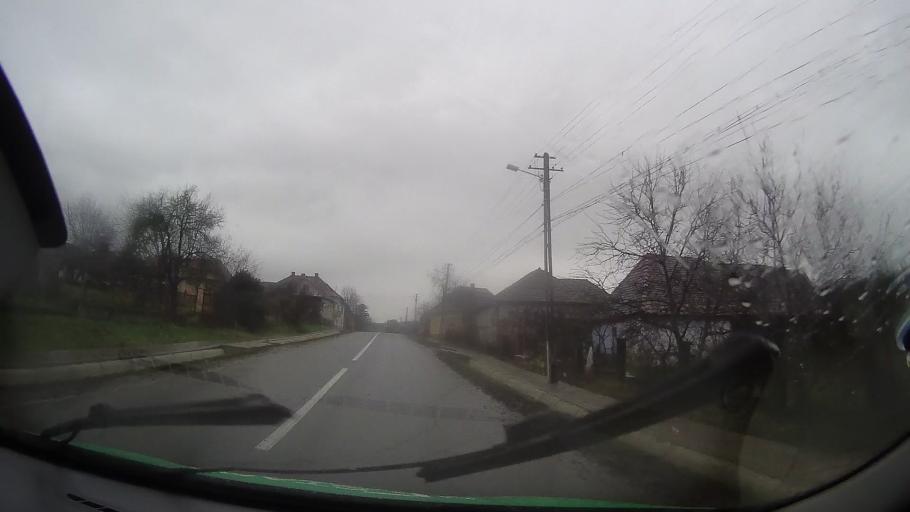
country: RO
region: Bistrita-Nasaud
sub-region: Comuna Monor
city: Monor
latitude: 46.9513
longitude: 24.6858
